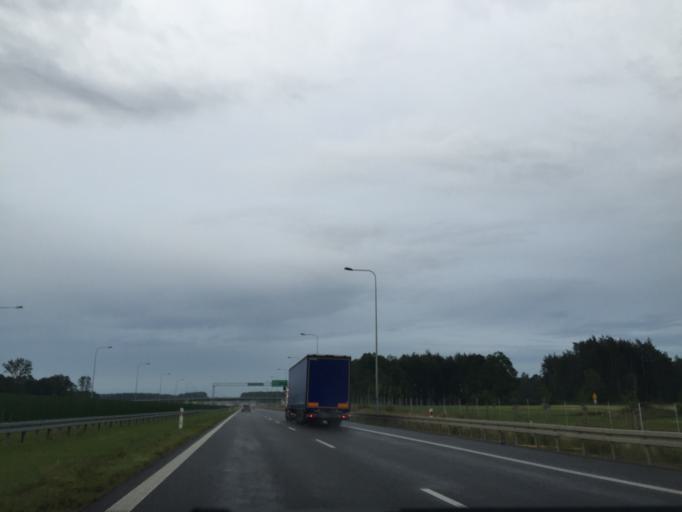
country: PL
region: Podlasie
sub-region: Powiat zambrowski
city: Rutki-Kossaki
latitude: 53.0336
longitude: 22.3451
